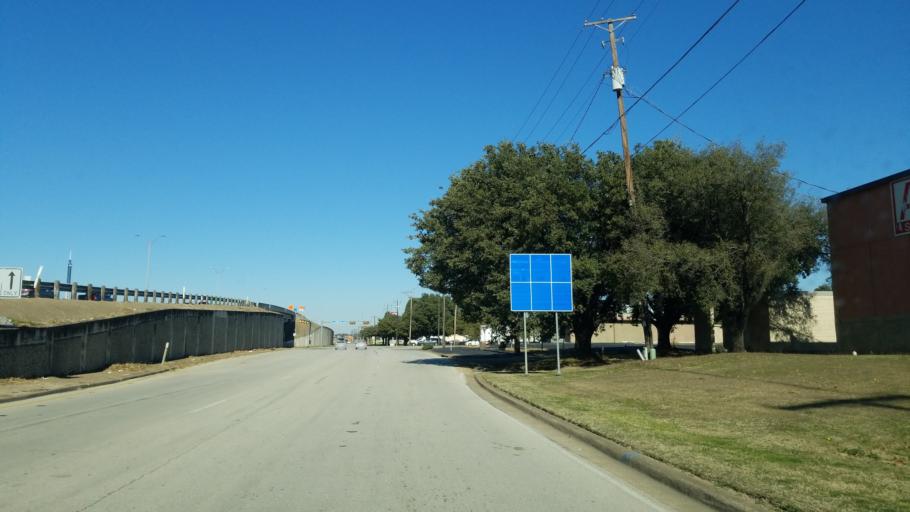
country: US
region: Texas
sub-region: Tarrant County
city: Arlington
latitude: 32.7475
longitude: -97.0622
